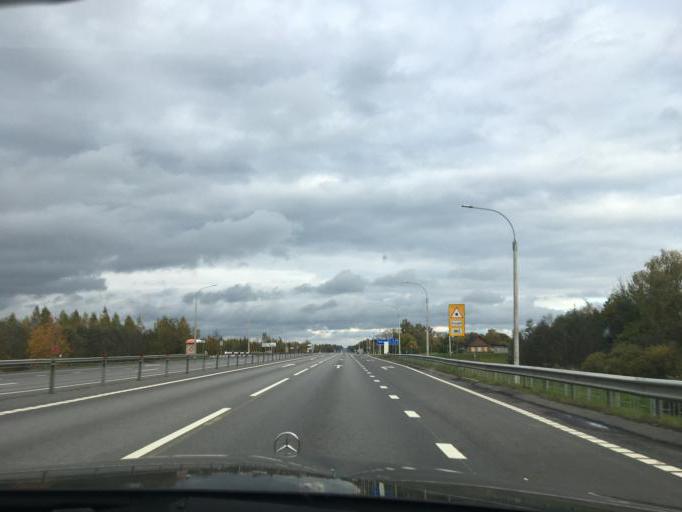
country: BY
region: Vitebsk
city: Dubrowna
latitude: 54.6892
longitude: 30.8862
